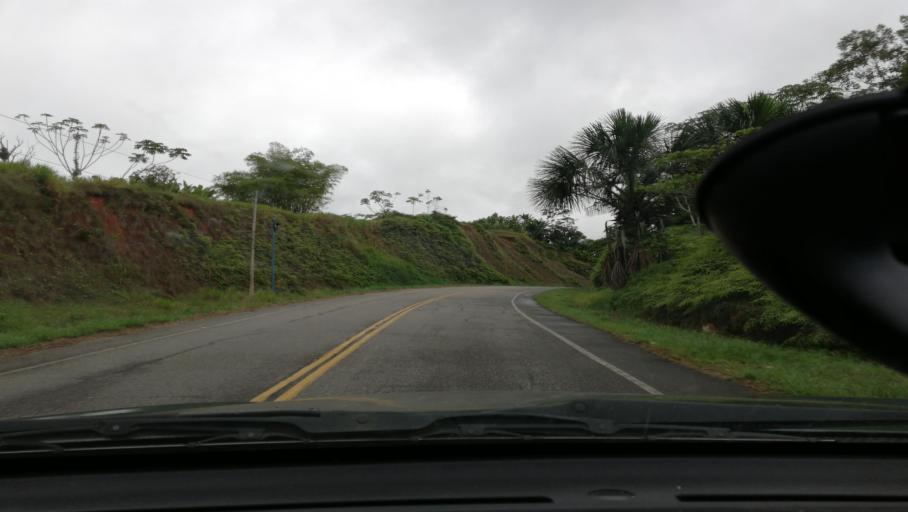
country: PE
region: Loreto
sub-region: Provincia de Loreto
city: Nauta
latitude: -4.4798
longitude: -73.5955
